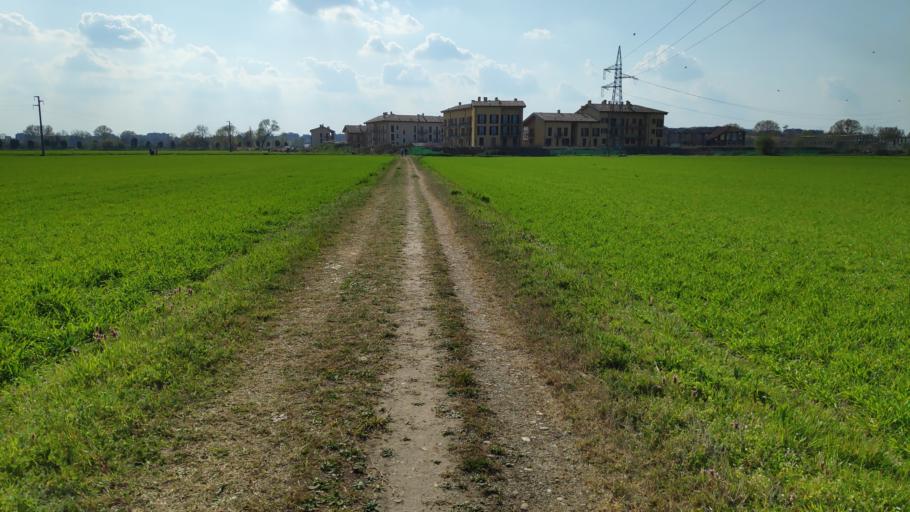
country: IT
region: Lombardy
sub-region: Citta metropolitana di Milano
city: San Giuliano Milanese
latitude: 45.4131
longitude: 9.2894
